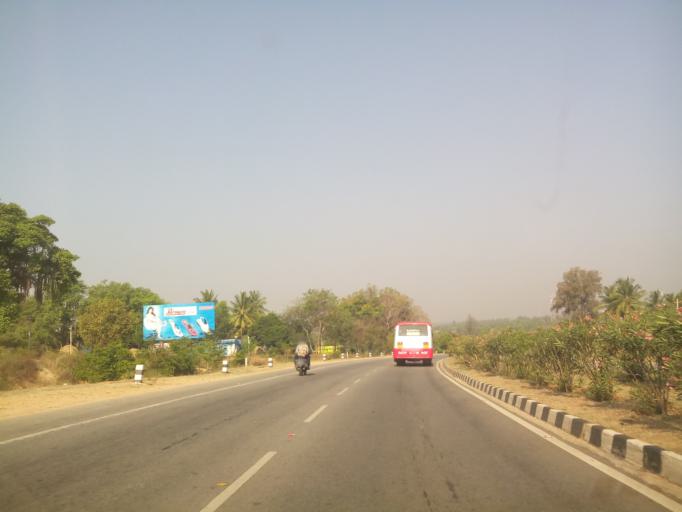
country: IN
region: Karnataka
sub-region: Bangalore Rural
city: Nelamangala
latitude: 13.0606
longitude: 77.3361
